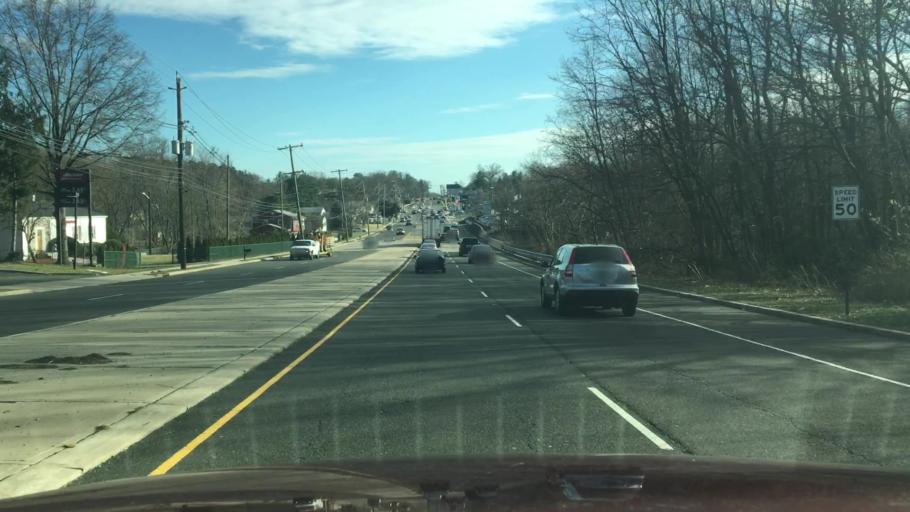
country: US
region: New Jersey
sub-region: Middlesex County
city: Milltown
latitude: 40.4597
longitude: -74.4253
